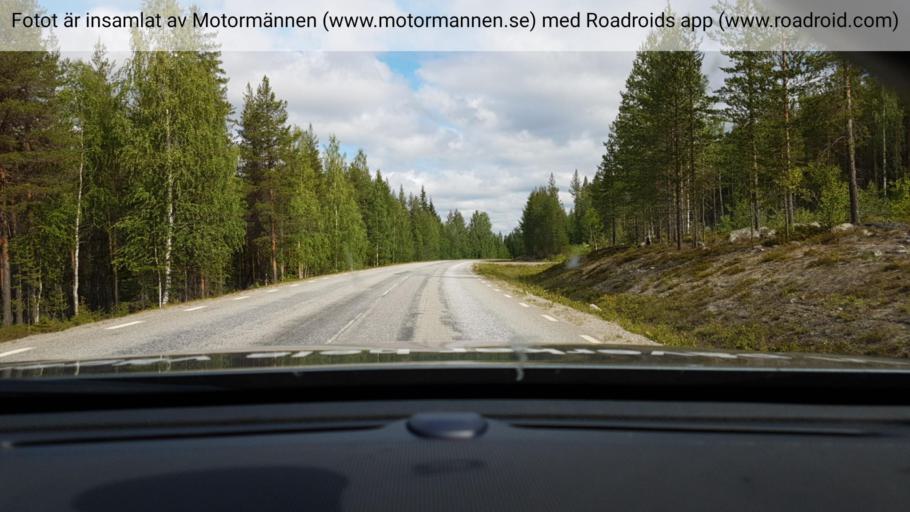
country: SE
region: Vaesterbotten
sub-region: Lycksele Kommun
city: Lycksele
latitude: 64.8634
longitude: 18.7213
